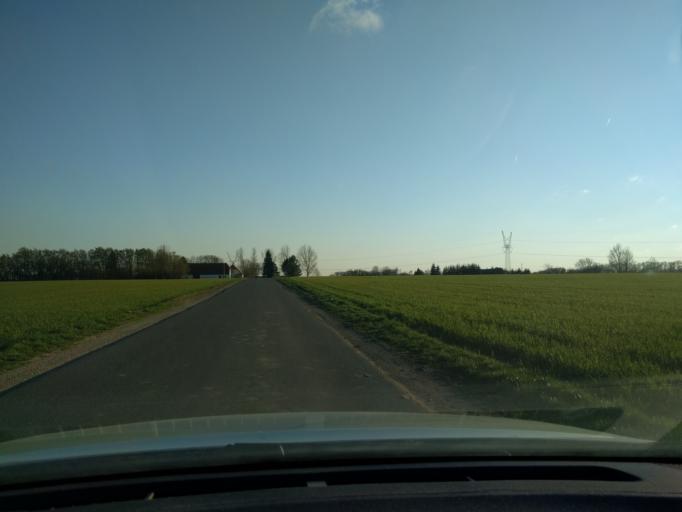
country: DK
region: South Denmark
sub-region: Odense Kommune
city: Bullerup
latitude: 55.3887
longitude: 10.5137
